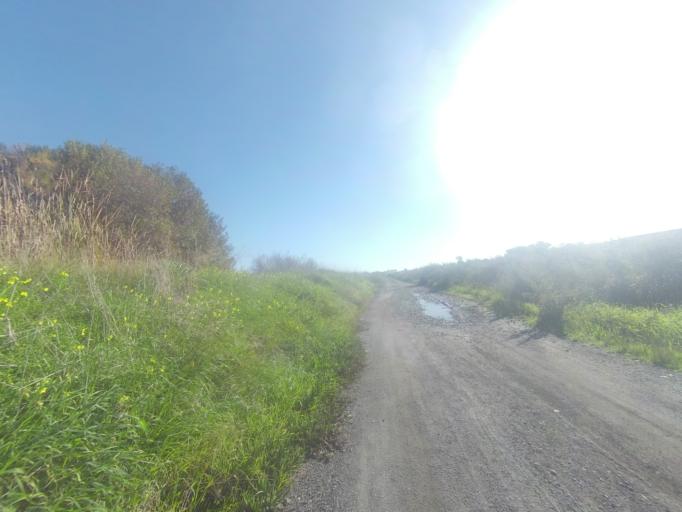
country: ES
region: Andalusia
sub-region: Provincia de Huelva
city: Palos de la Frontera
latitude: 37.2563
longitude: -6.9129
